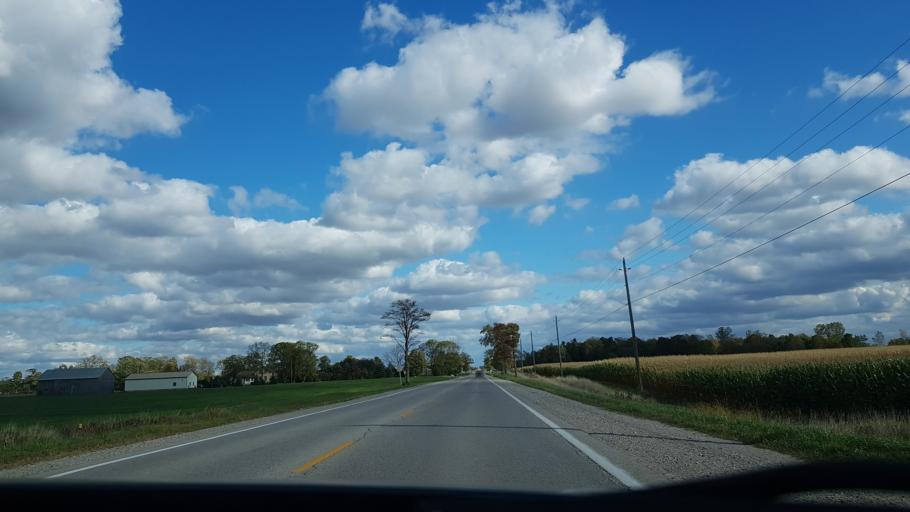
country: CA
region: Ontario
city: South Huron
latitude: 43.1518
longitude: -81.6783
